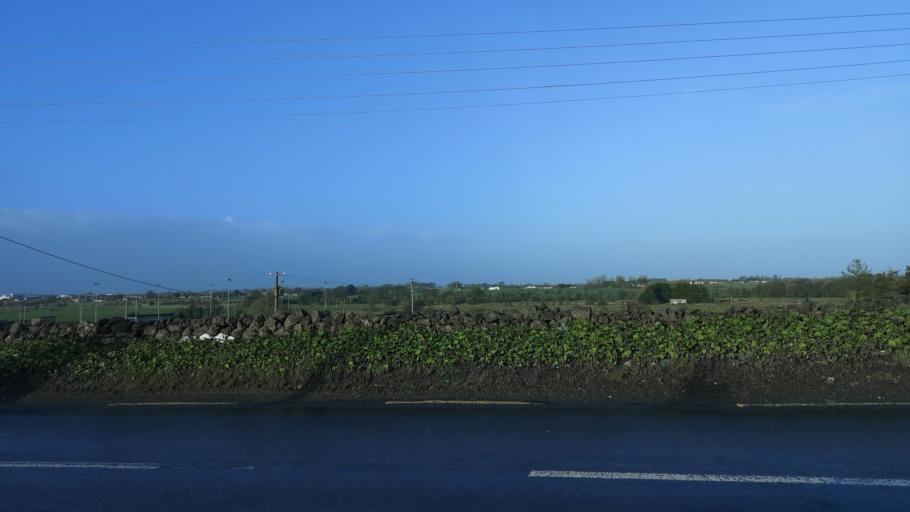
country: IE
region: Connaught
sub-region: County Galway
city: Tuam
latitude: 53.5066
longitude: -8.8313
